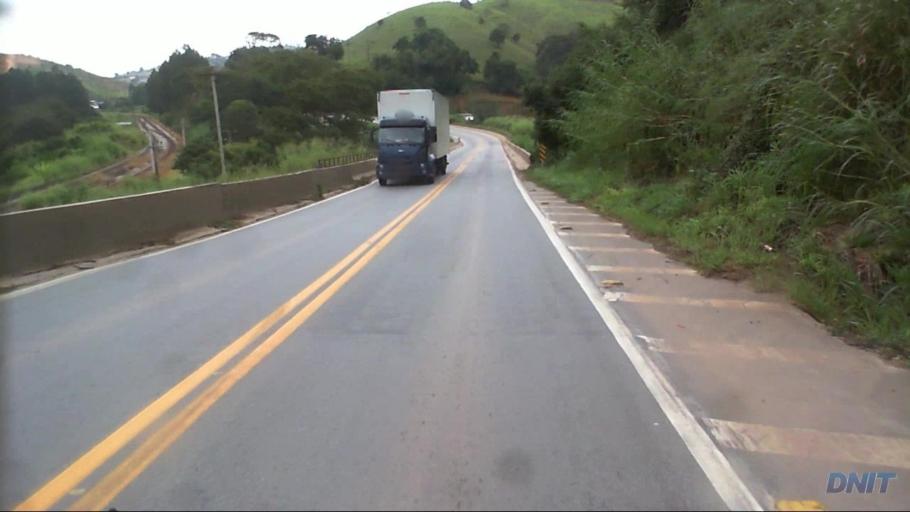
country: BR
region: Minas Gerais
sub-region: Nova Era
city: Nova Era
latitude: -19.7427
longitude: -43.0202
